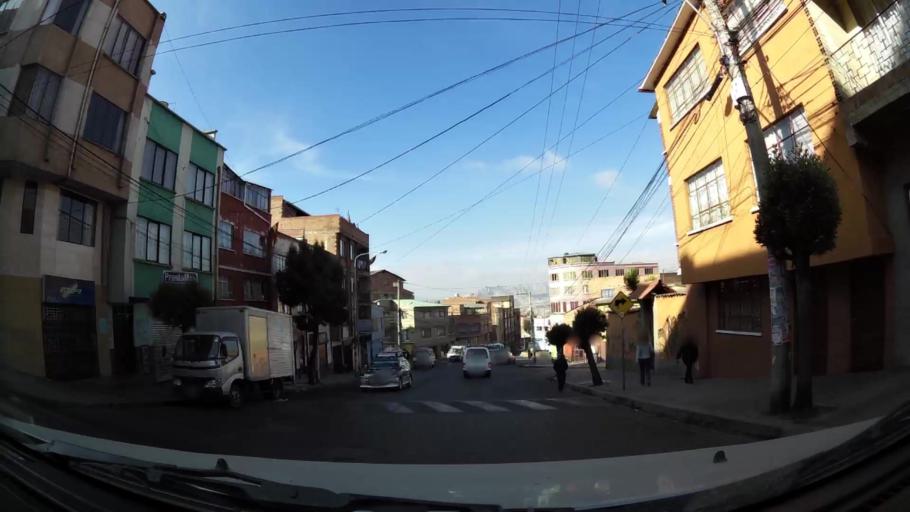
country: BO
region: La Paz
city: La Paz
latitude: -16.4949
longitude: -68.1153
